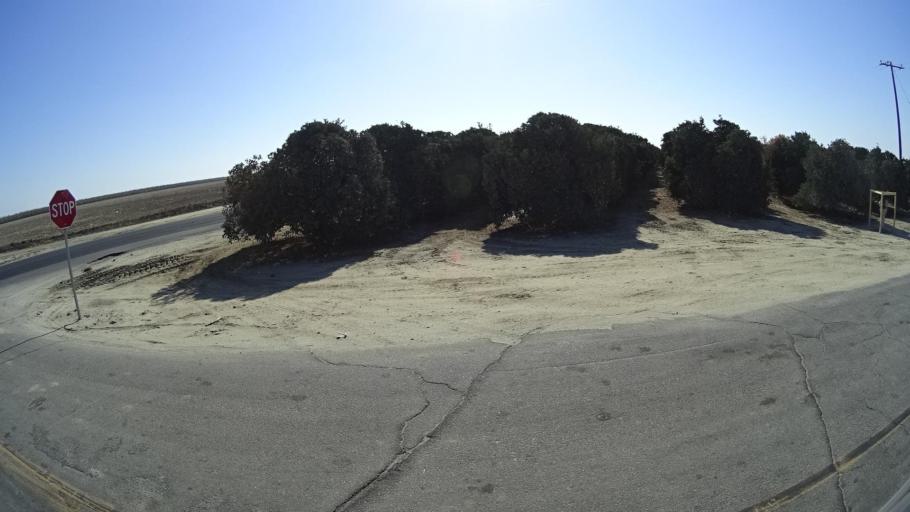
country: US
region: California
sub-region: Kern County
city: McFarland
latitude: 35.7035
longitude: -119.1688
